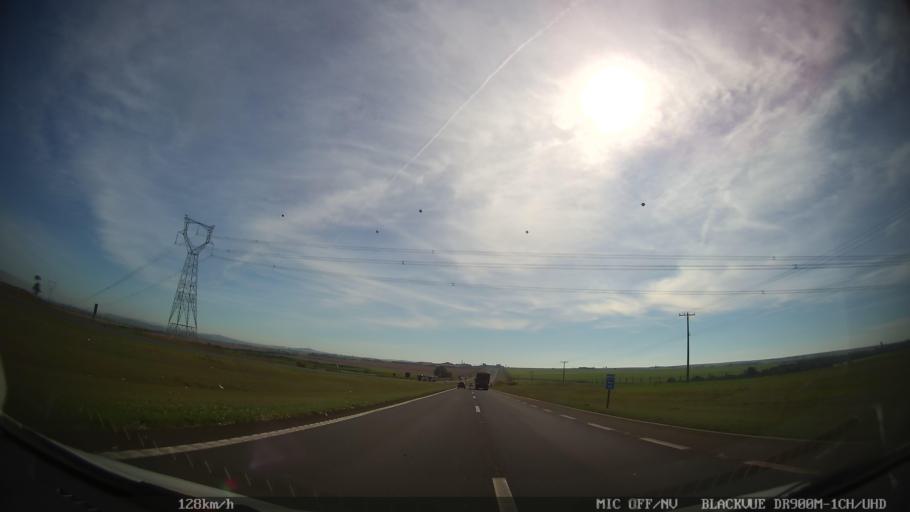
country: BR
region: Sao Paulo
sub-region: Araras
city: Araras
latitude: -22.4339
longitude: -47.3953
